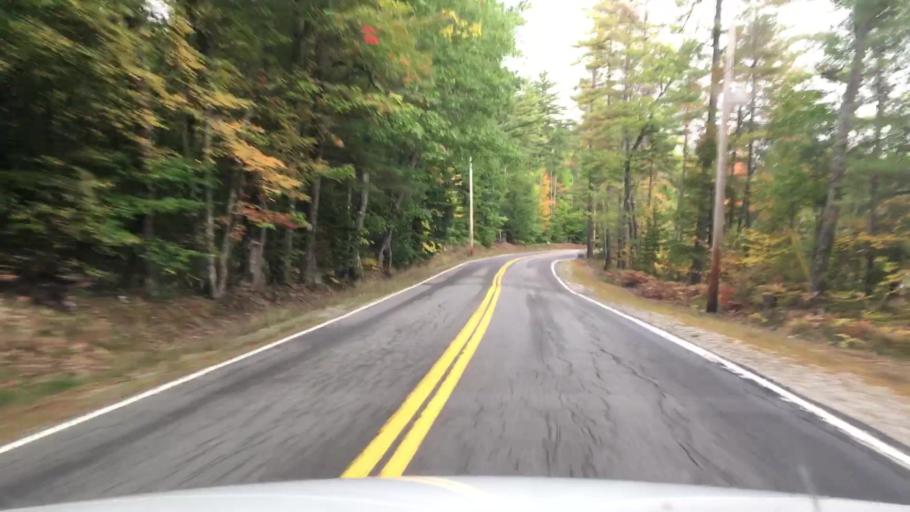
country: US
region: Maine
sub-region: Oxford County
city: Bethel
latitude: 44.3544
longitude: -70.7920
